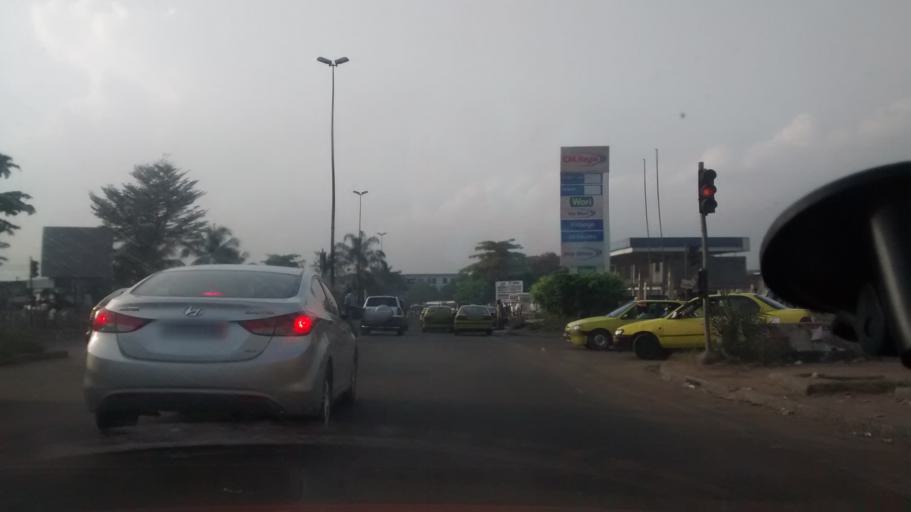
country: CI
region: Lagunes
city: Abobo
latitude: 5.3687
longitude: -3.9983
